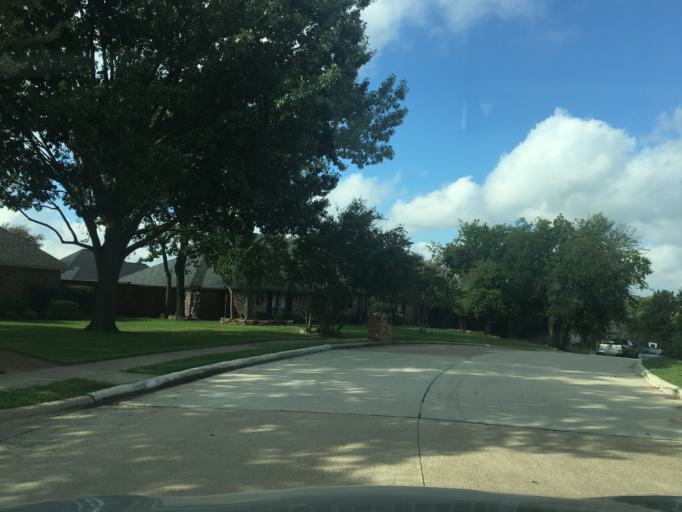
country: US
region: Texas
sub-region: Dallas County
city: Sachse
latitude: 32.9684
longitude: -96.5919
